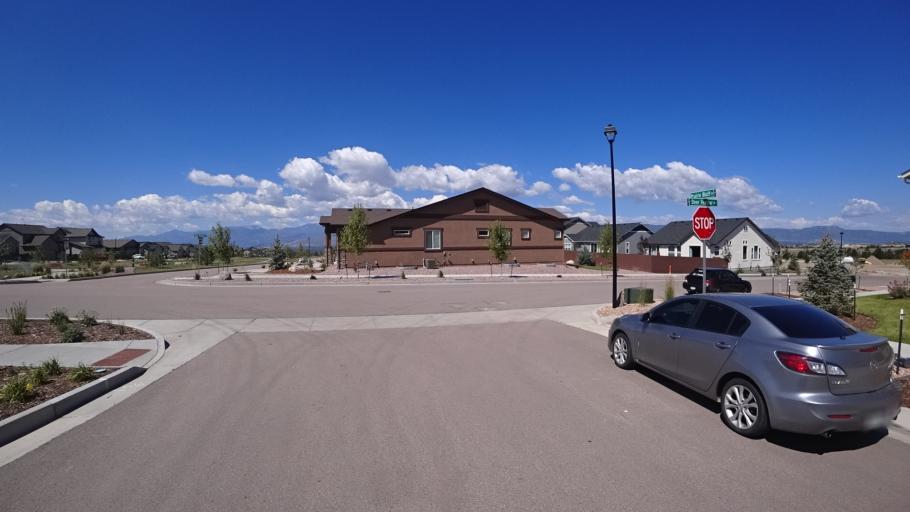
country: US
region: Colorado
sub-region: El Paso County
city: Black Forest
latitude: 38.9934
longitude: -104.7636
